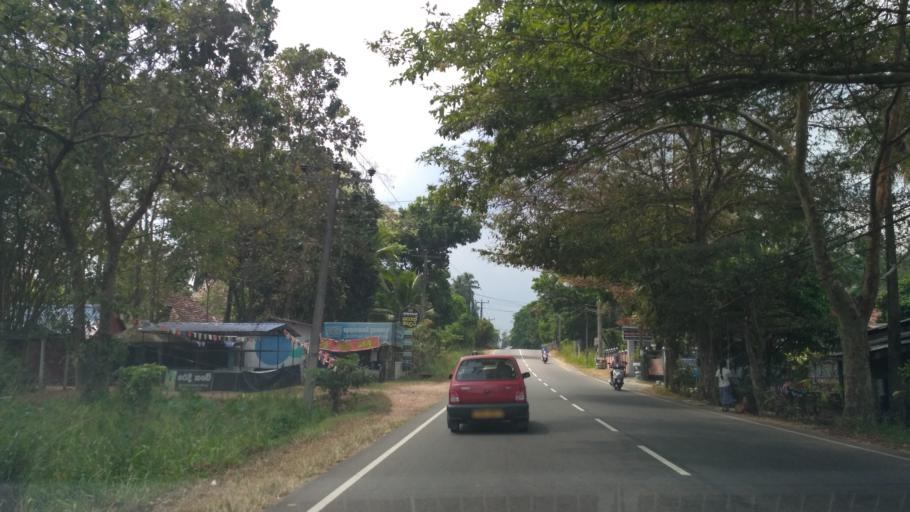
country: LK
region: North Western
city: Kuliyapitiya
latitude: 7.3250
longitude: 80.1084
